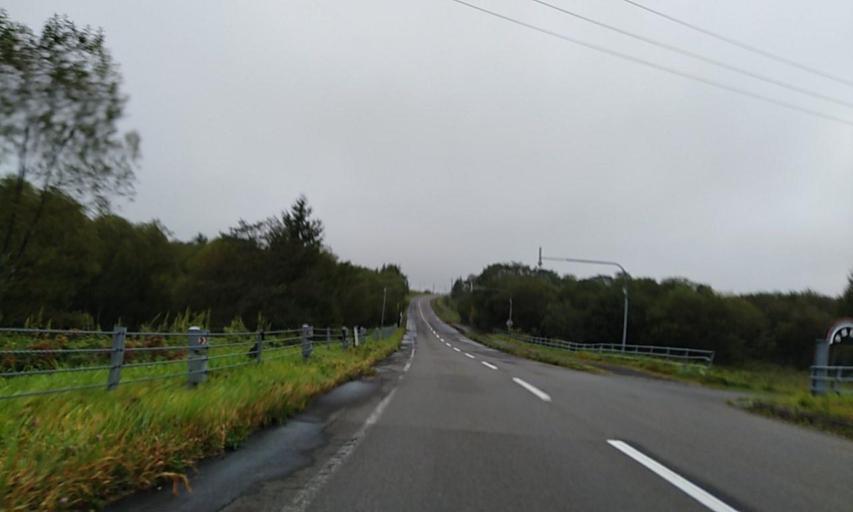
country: JP
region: Hokkaido
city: Shibetsu
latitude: 43.4892
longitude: 144.6381
